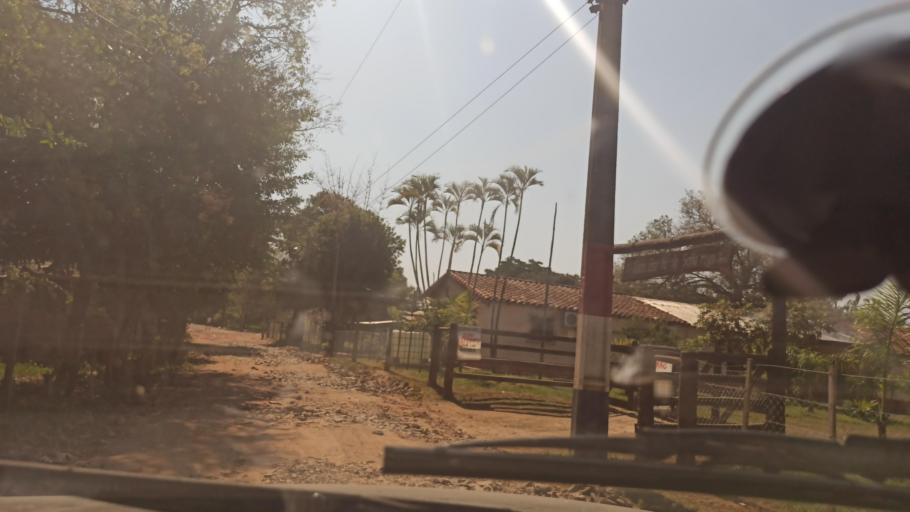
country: AR
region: Formosa
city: Clorinda
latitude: -25.3081
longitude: -57.6975
